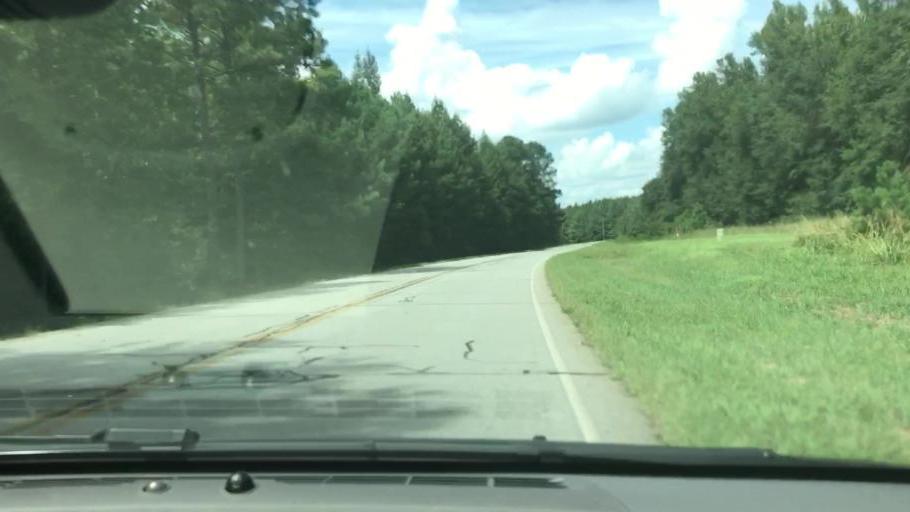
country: US
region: Georgia
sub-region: Stewart County
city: Lumpkin
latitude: 32.1483
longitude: -84.8992
